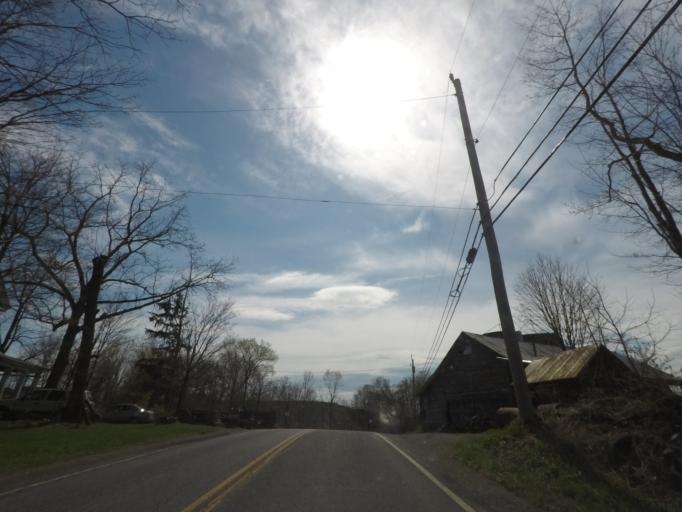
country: US
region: New York
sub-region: Columbia County
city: Chatham
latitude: 42.3572
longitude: -73.5377
